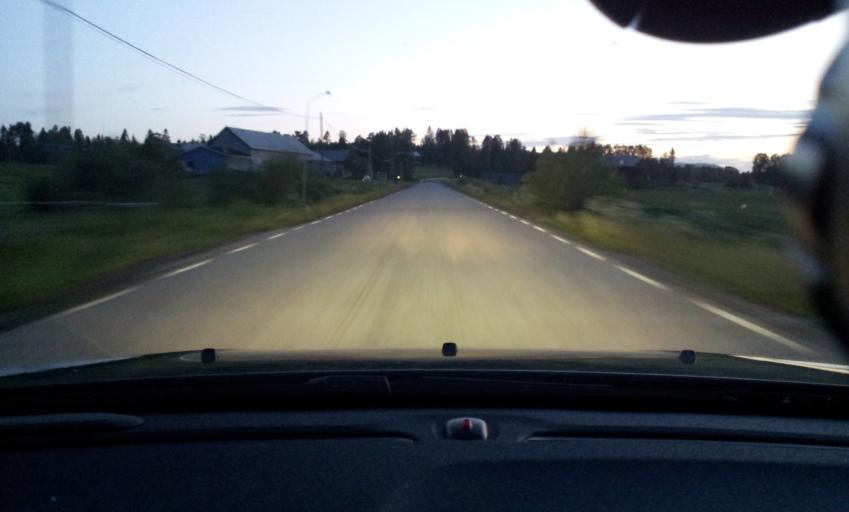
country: SE
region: Jaemtland
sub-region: Bergs Kommun
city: Hoverberg
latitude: 62.7744
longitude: 14.5245
